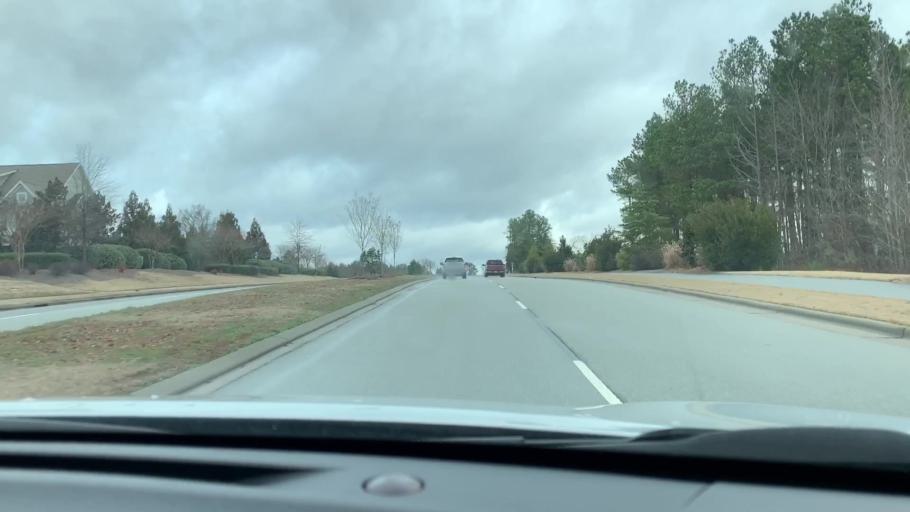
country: US
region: North Carolina
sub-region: Wake County
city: Green Level
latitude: 35.8390
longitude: -78.8996
